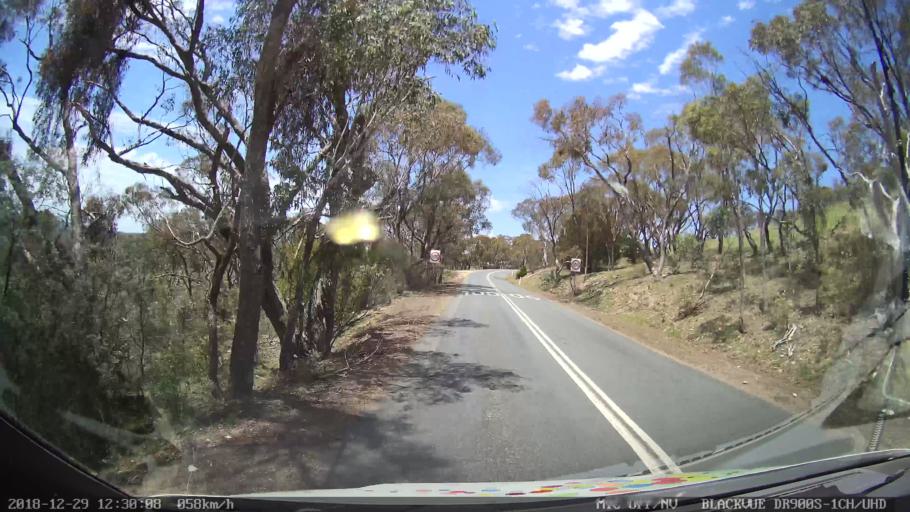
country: AU
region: Australian Capital Territory
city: Macarthur
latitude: -35.5034
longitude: 149.2330
